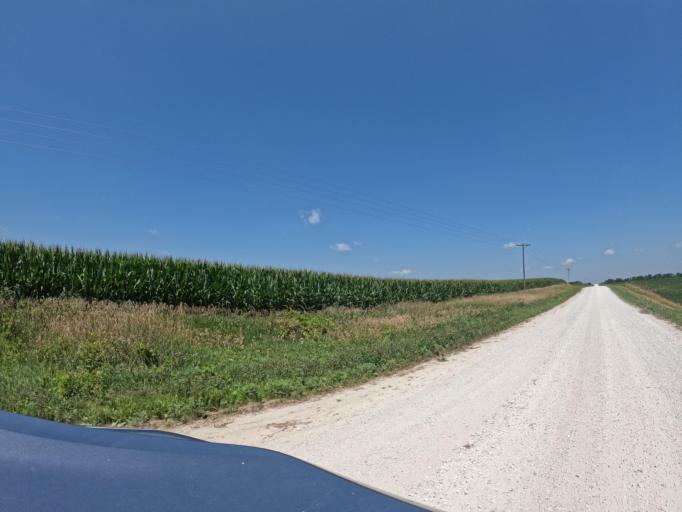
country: US
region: Iowa
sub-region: Keokuk County
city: Sigourney
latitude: 41.2763
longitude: -92.2381
